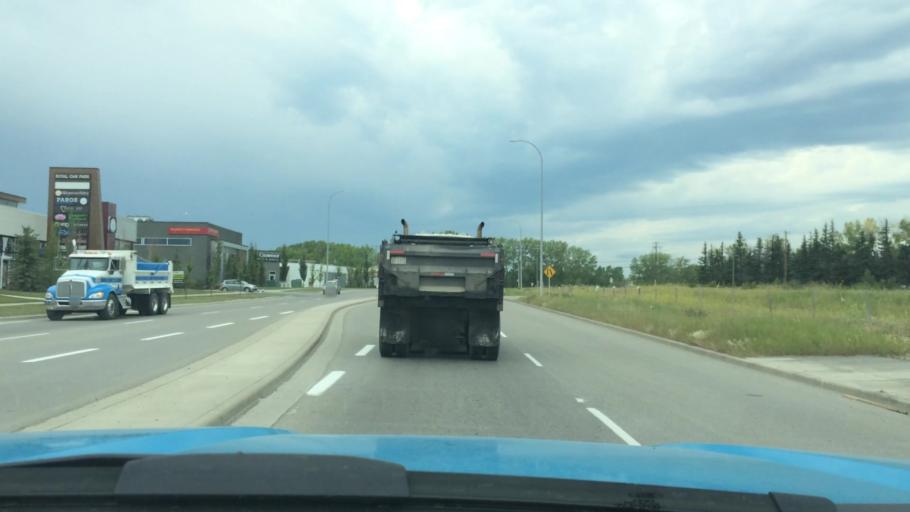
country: CA
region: Alberta
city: Calgary
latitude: 51.1526
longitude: -114.2096
